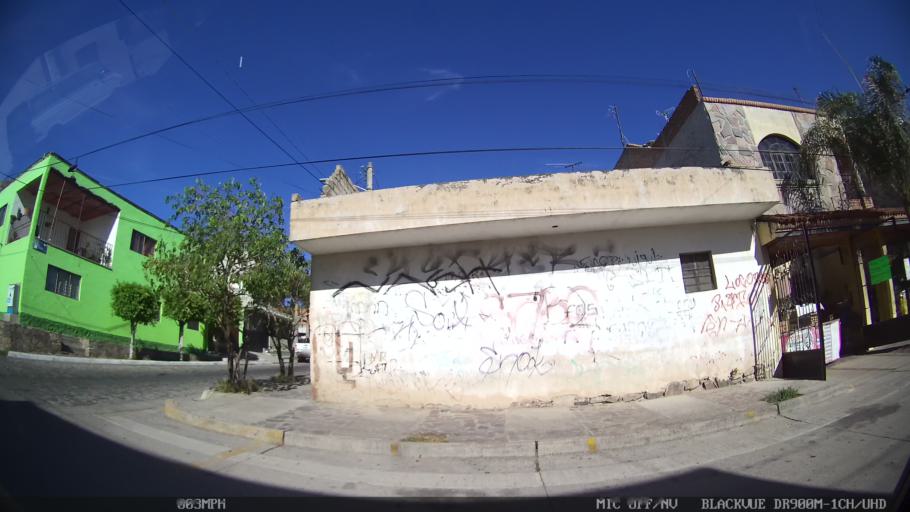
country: MX
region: Jalisco
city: Tlaquepaque
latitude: 20.6954
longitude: -103.2791
